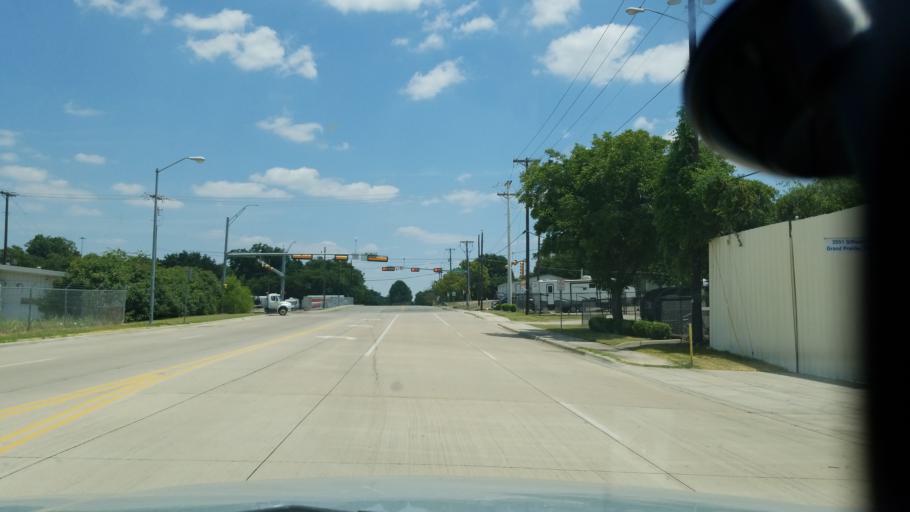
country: US
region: Texas
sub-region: Dallas County
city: Grand Prairie
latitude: 32.7602
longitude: -96.9610
